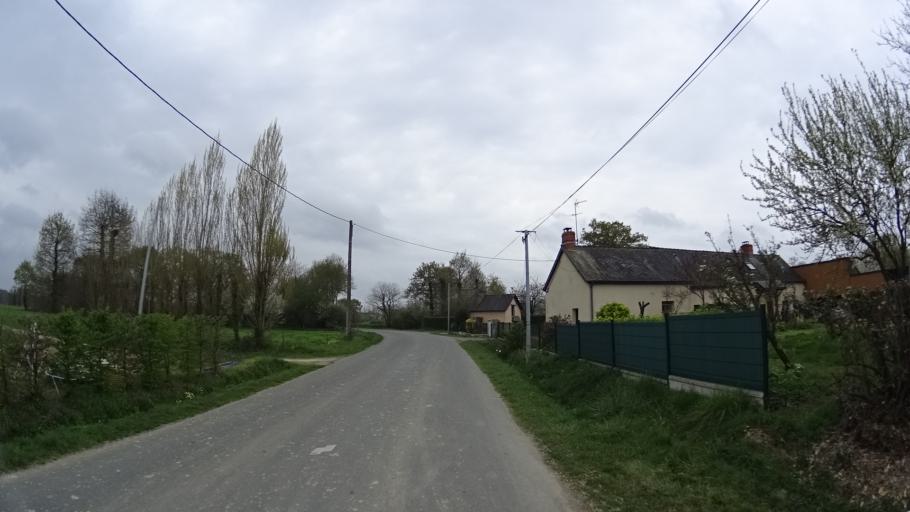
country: FR
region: Brittany
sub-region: Departement d'Ille-et-Vilaine
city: La Chapelle-Thouarault
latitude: 48.1176
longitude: -1.8717
